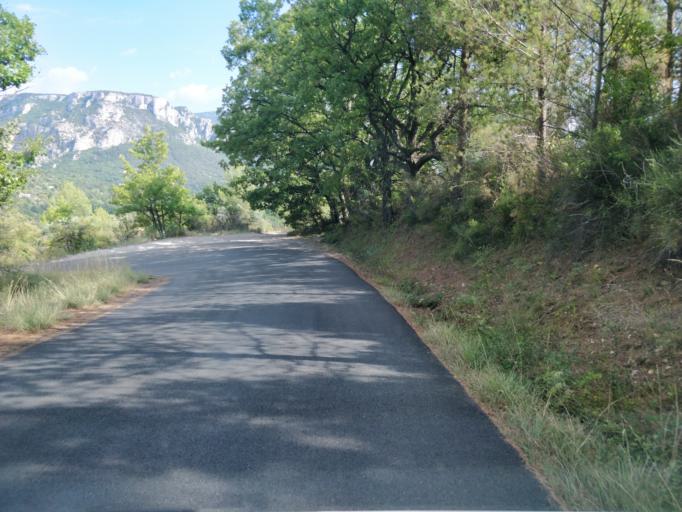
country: FR
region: Provence-Alpes-Cote d'Azur
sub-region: Departement des Alpes-de-Haute-Provence
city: Riez
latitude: 43.8393
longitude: 6.2062
